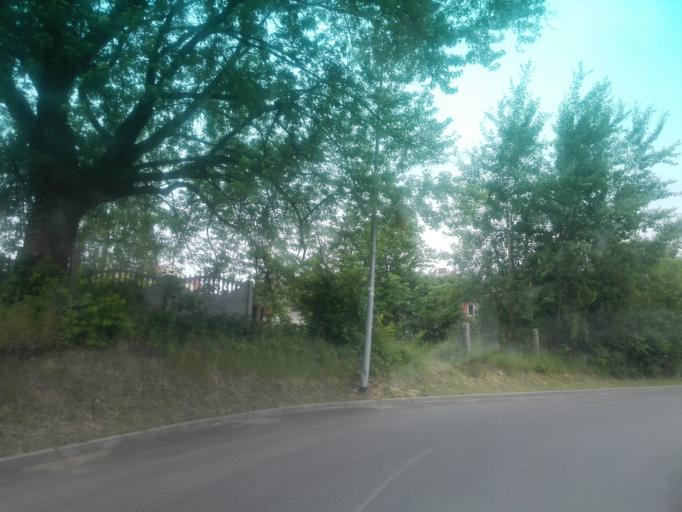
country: PL
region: Silesian Voivodeship
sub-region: Powiat czestochowski
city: Olsztyn
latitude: 50.7532
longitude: 19.2686
